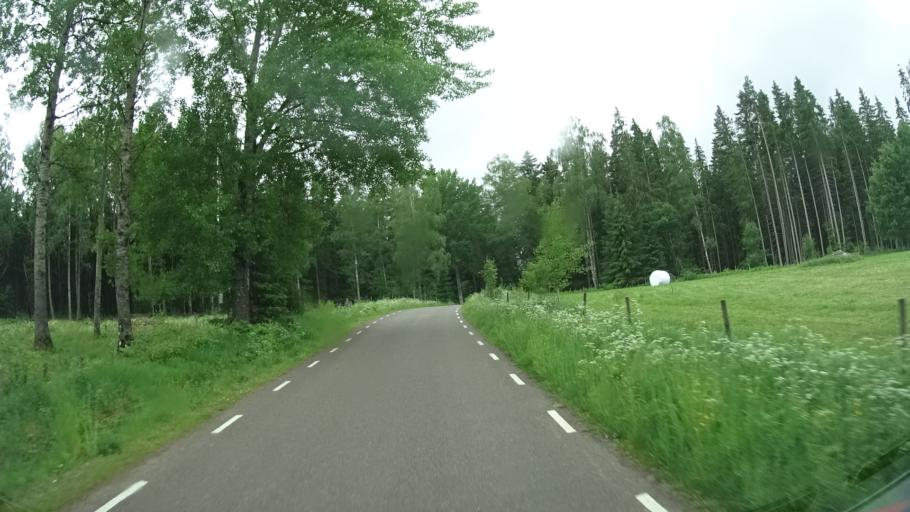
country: SE
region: Kalmar
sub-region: Vimmerby Kommun
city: Sodra Vi
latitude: 57.6881
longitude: 15.6857
